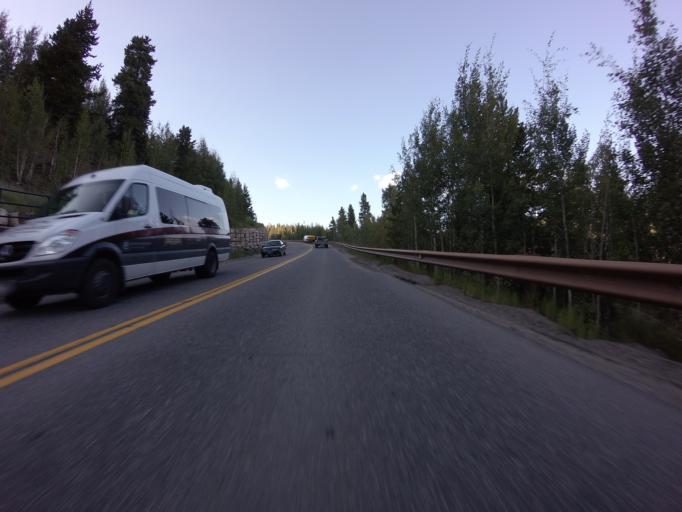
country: US
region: Colorado
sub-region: Summit County
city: Breckenridge
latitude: 39.4847
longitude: -106.0520
